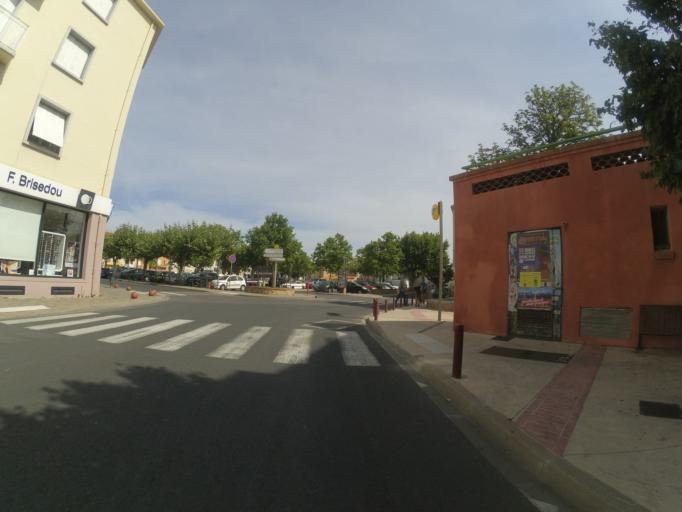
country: FR
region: Languedoc-Roussillon
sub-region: Departement des Pyrenees-Orientales
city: Ille-sur-Tet
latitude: 42.6700
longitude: 2.6224
